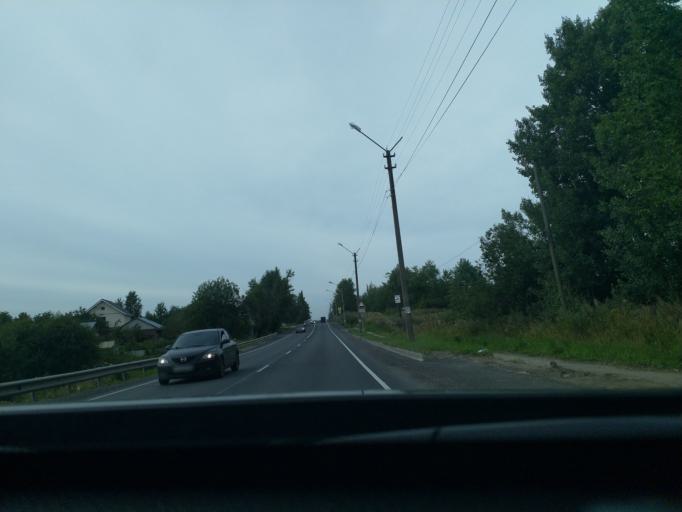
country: RU
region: Leningrad
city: Nikol'skoye
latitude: 59.7141
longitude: 30.7794
